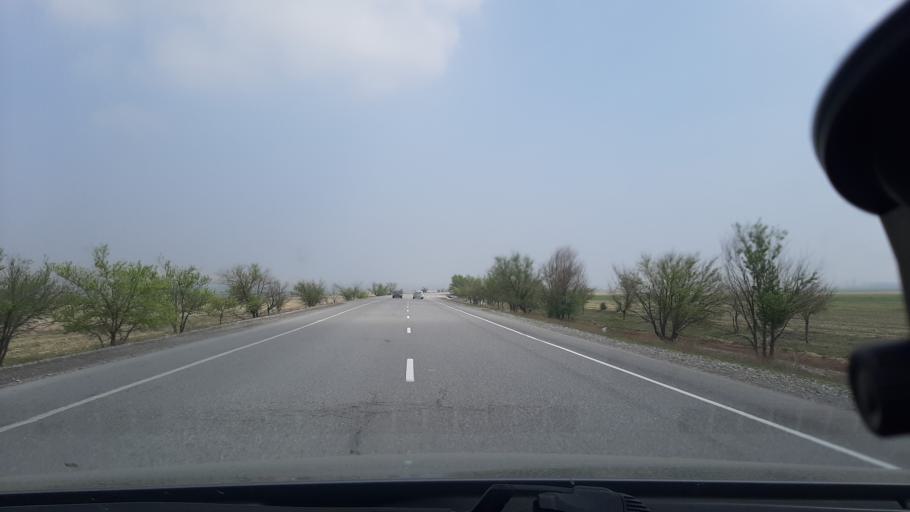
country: UZ
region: Toshkent
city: Bekobod
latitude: 40.1132
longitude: 69.1954
